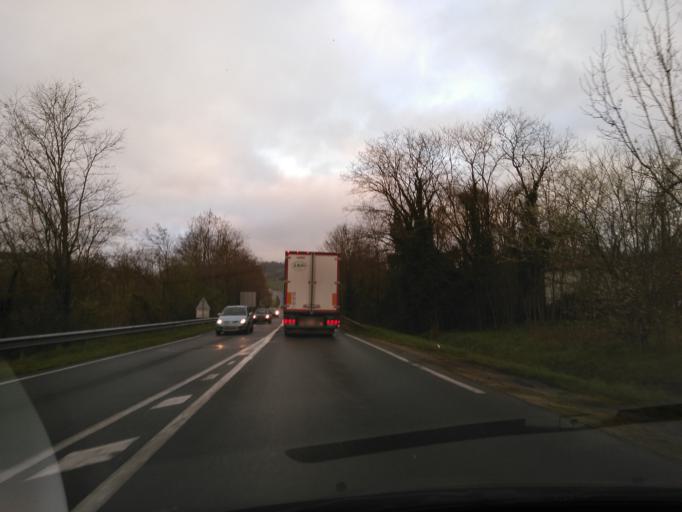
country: FR
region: Aquitaine
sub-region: Departement du Lot-et-Garonne
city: Villeneuve-sur-Lot
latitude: 44.4307
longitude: 0.7297
